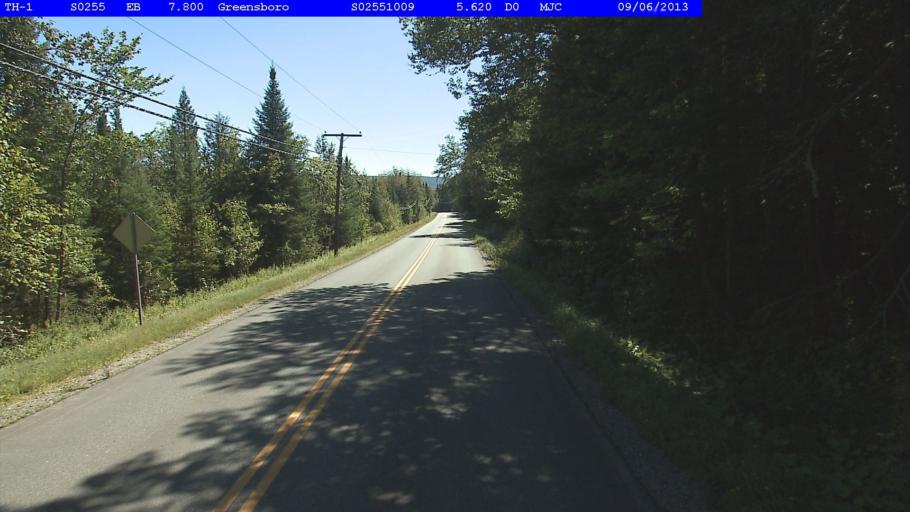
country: US
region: Vermont
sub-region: Caledonia County
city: Hardwick
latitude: 44.5698
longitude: -72.2898
